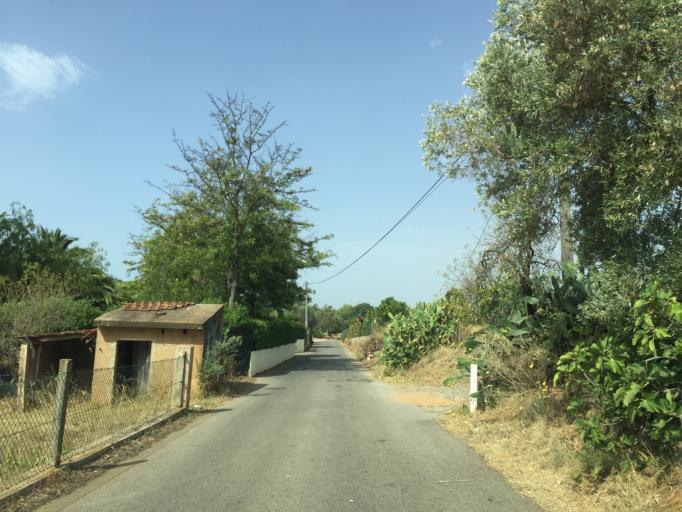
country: PT
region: Faro
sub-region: Loule
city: Vilamoura
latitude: 37.1052
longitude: -8.1077
